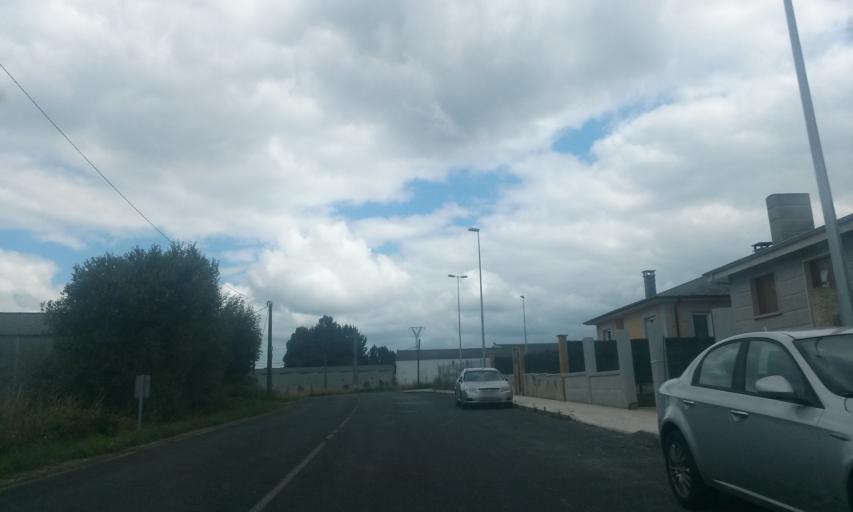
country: ES
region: Galicia
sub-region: Provincia de Lugo
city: Outeiro de Rei
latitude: 43.0612
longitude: -7.6121
